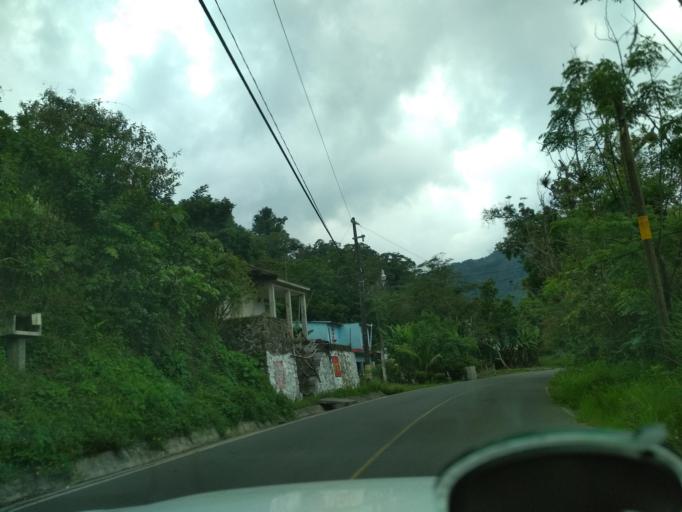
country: MX
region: Veracruz
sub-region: Jilotepec
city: El Pueblito (Garbanzal)
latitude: 19.6156
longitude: -96.9272
